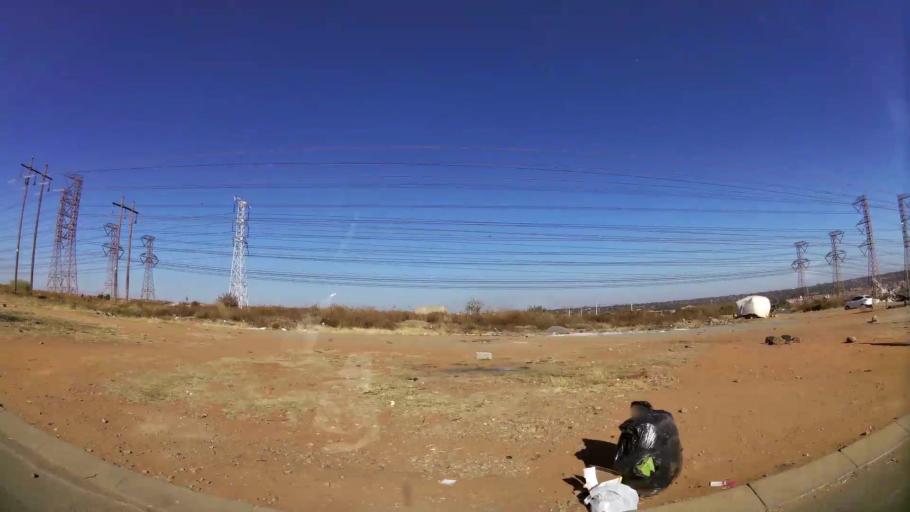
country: ZA
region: Gauteng
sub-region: Ekurhuleni Metropolitan Municipality
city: Tembisa
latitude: -26.0293
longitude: 28.2227
